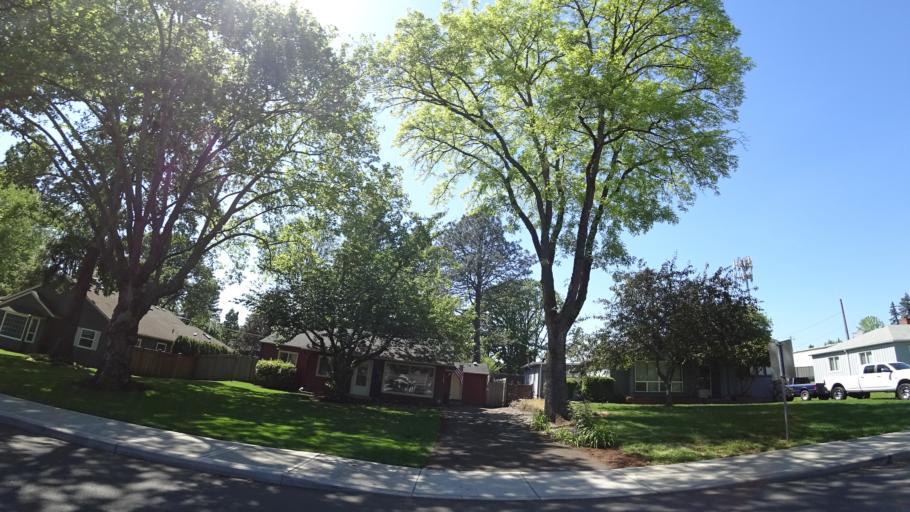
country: US
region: Oregon
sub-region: Washington County
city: Cedar Hills
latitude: 45.4998
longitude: -122.8039
